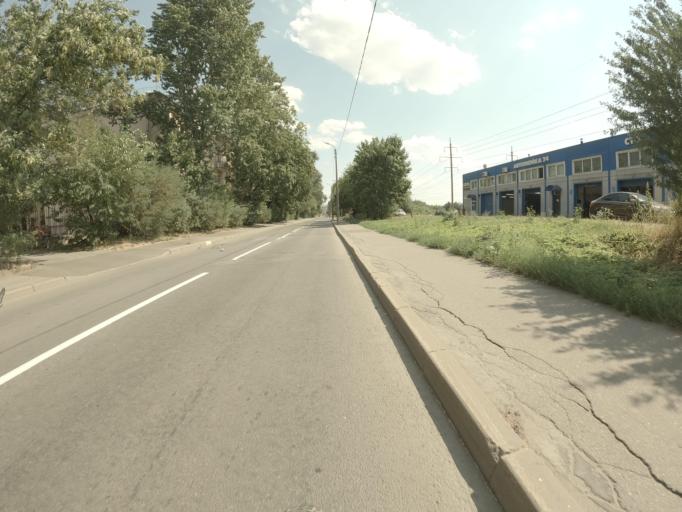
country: RU
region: St.-Petersburg
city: Avtovo
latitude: 59.8891
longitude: 30.2606
